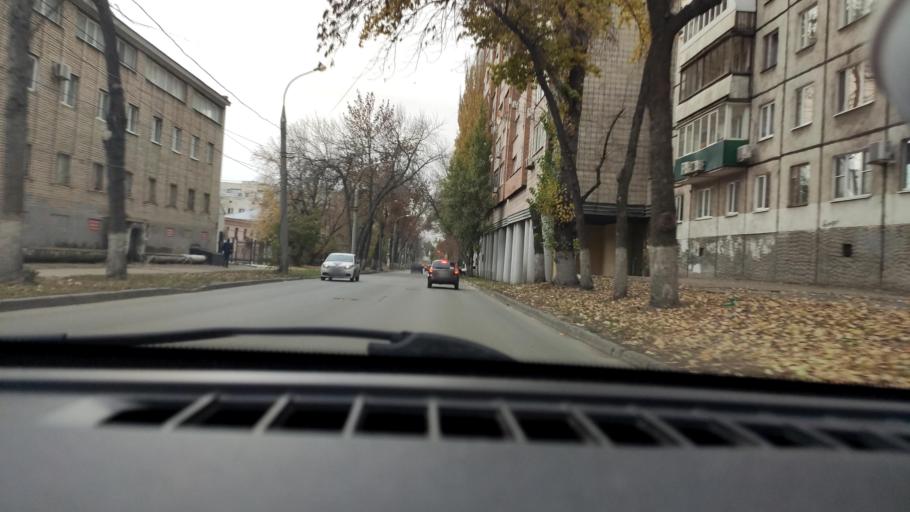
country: RU
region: Samara
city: Samara
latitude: 53.2031
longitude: 50.1319
